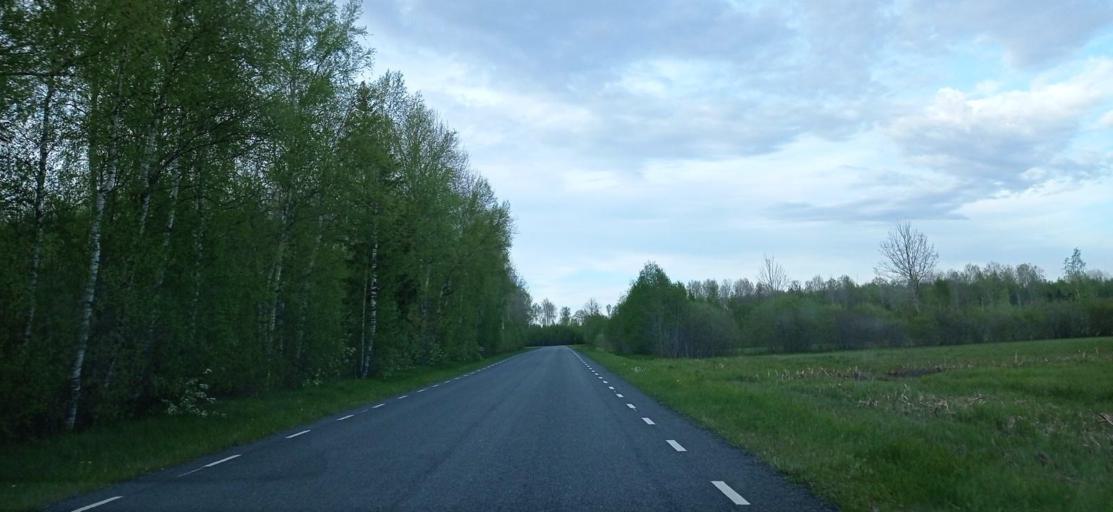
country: EE
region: Paernumaa
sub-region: Tootsi vald
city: Tootsi
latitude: 58.5643
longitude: 24.8054
